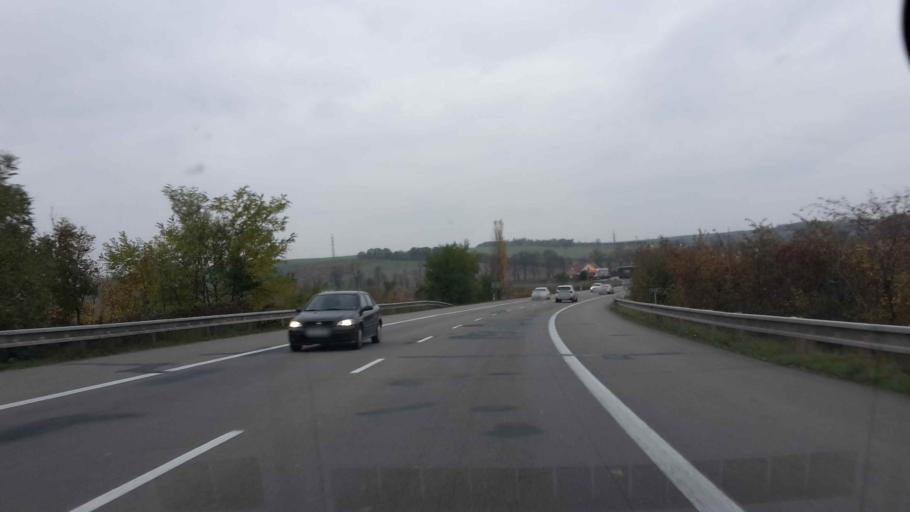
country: CZ
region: South Moravian
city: Slavkov u Brna
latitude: 49.1477
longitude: 16.8672
